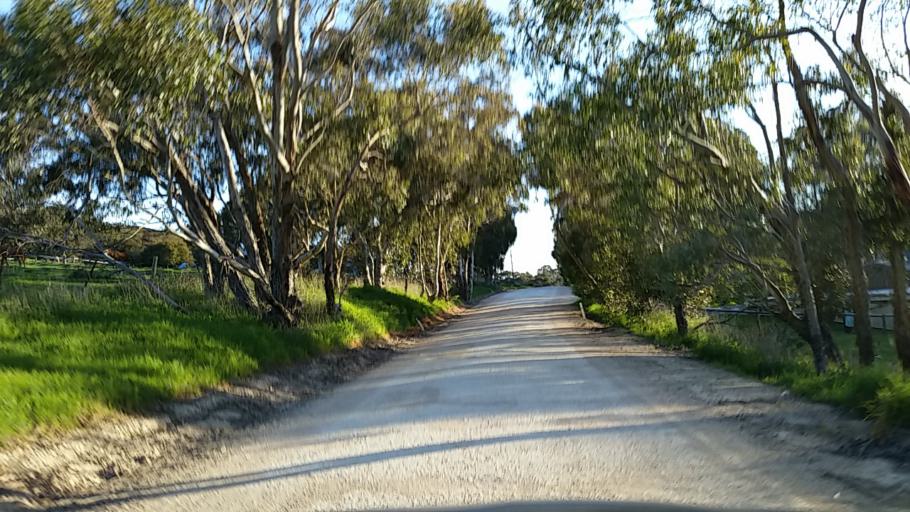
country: AU
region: South Australia
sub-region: Alexandrina
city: Mount Compass
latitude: -35.2928
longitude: 138.6882
